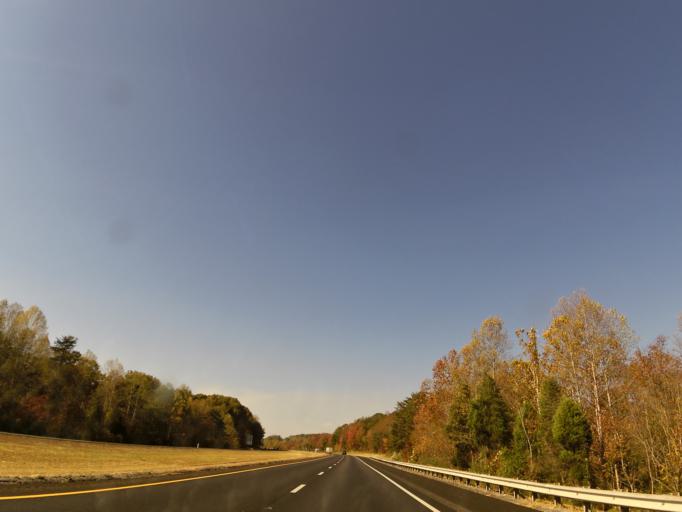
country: US
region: Tennessee
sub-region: Anderson County
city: Norris
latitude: 36.1846
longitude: -84.0966
